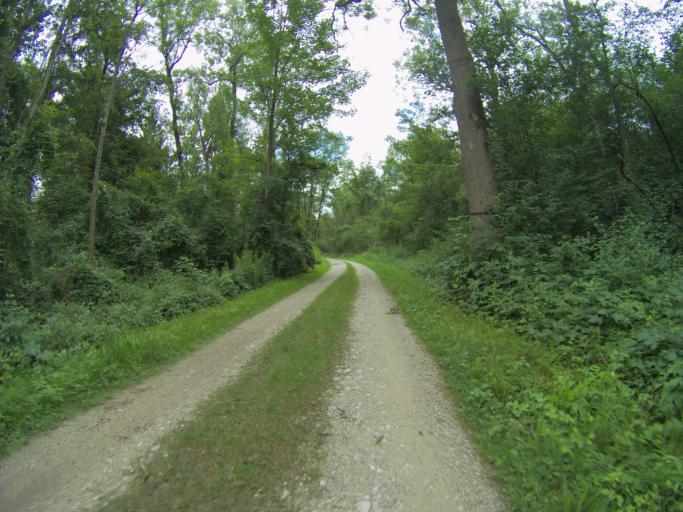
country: DE
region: Bavaria
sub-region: Upper Bavaria
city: Freising
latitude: 48.3717
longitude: 11.7387
